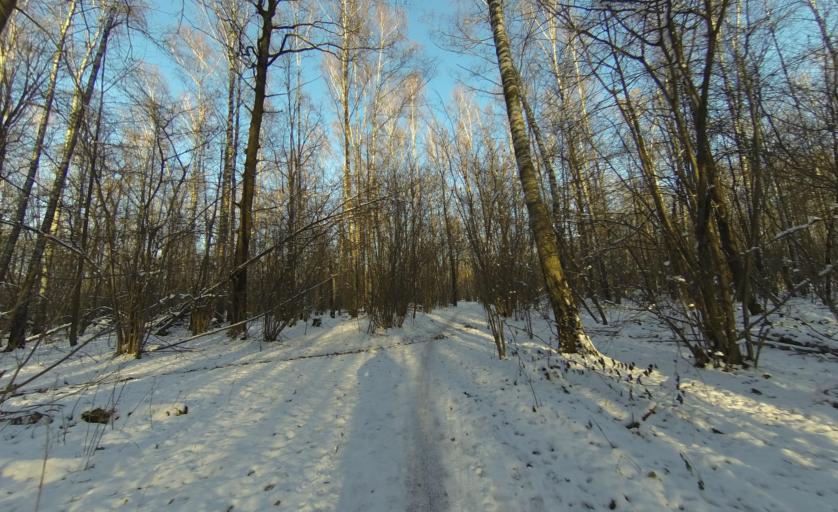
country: RU
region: Moscow
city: Rostokino
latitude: 55.8297
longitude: 37.6904
